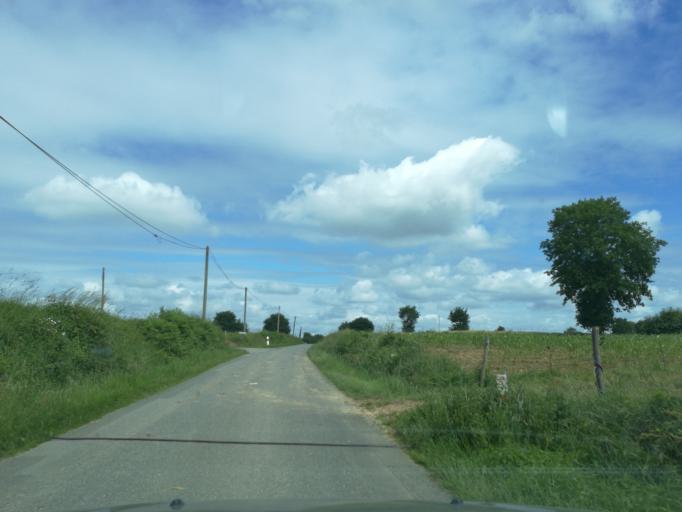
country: FR
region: Brittany
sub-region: Departement d'Ille-et-Vilaine
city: Bedee
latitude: 48.1964
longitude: -1.9910
